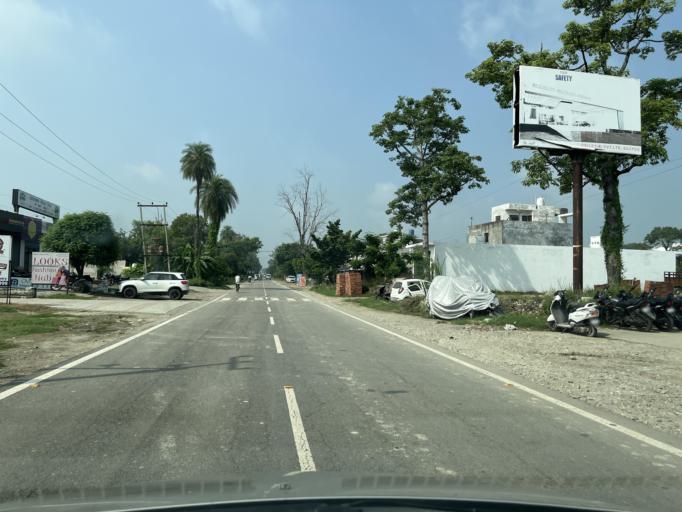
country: IN
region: Uttarakhand
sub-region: Udham Singh Nagar
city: Bazpur
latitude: 29.1707
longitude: 79.1659
